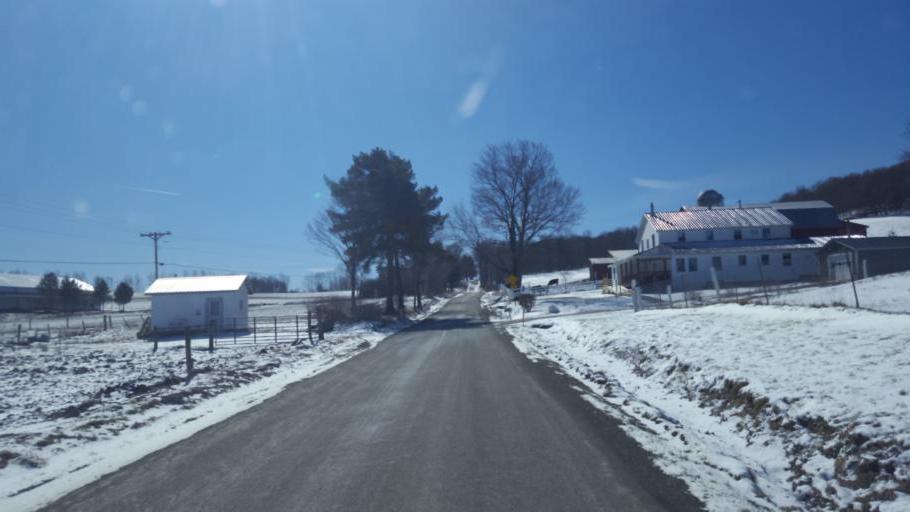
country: US
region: New York
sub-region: Allegany County
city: Andover
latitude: 41.9826
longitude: -77.7618
